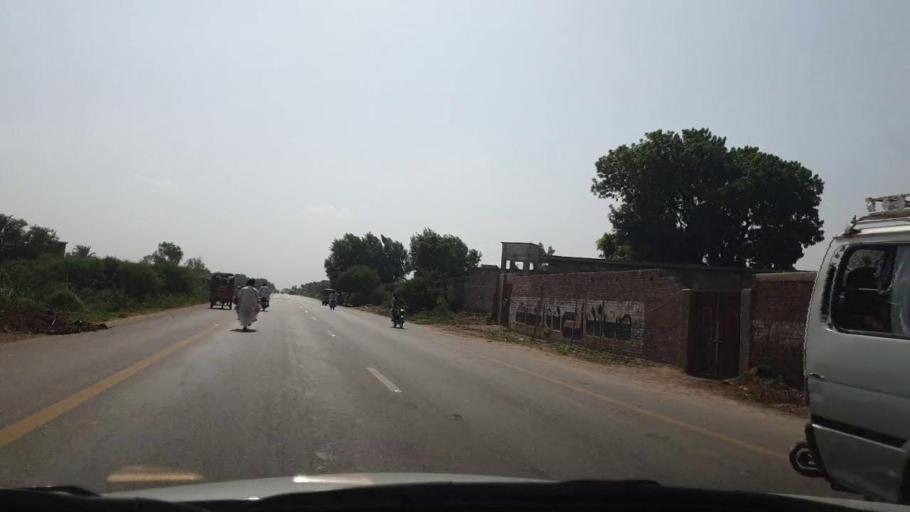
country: PK
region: Sindh
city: Matli
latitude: 25.0678
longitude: 68.6270
